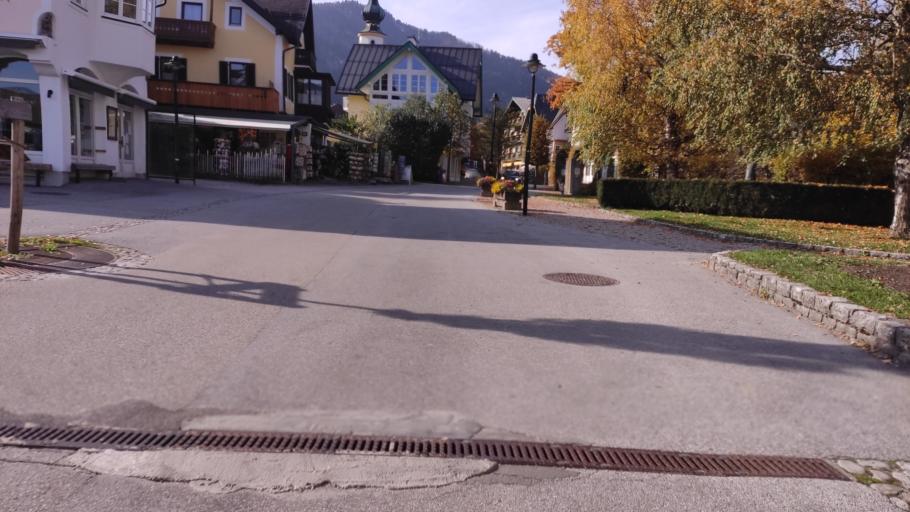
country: AT
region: Salzburg
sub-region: Politischer Bezirk Salzburg-Umgebung
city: Sankt Gilgen
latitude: 47.7666
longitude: 13.3677
